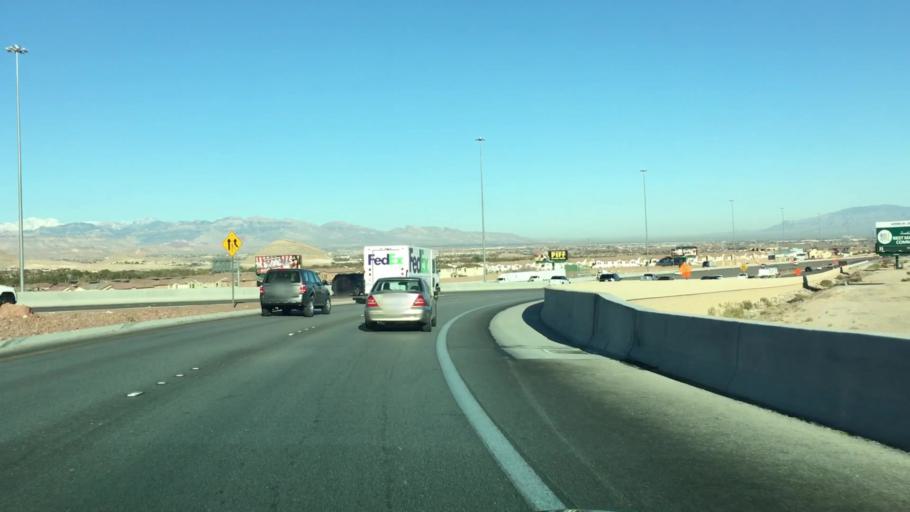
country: US
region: Nevada
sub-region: Clark County
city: Enterprise
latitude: 35.9641
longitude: -115.1804
